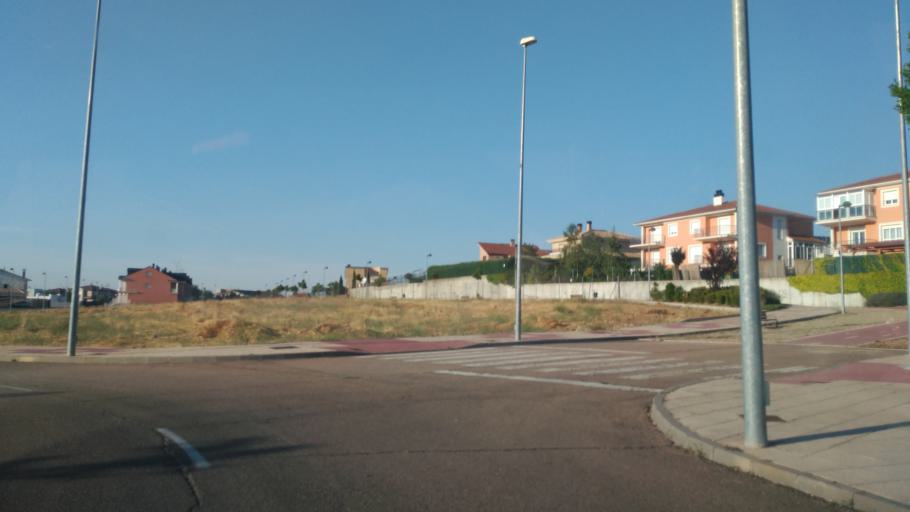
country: ES
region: Castille and Leon
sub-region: Provincia de Salamanca
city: Carbajosa de la Sagrada
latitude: 40.9375
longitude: -5.6445
